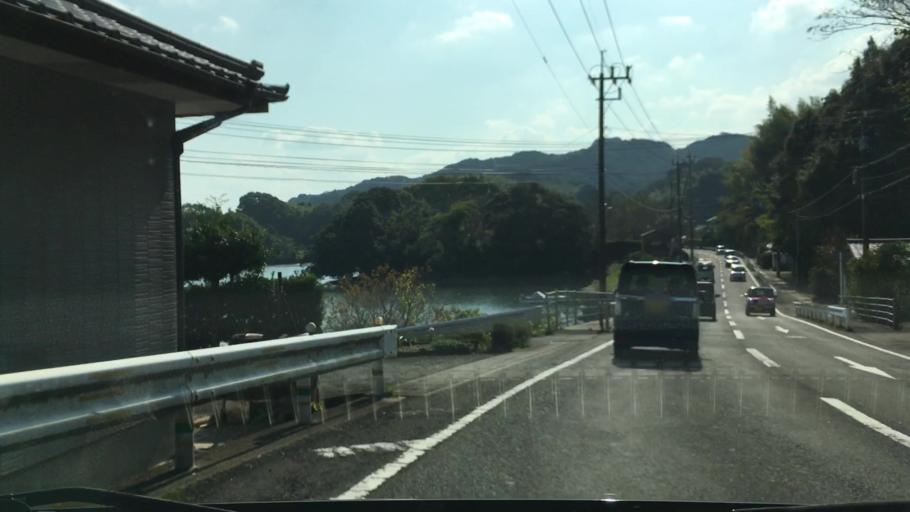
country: JP
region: Nagasaki
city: Togitsu
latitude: 32.9362
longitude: 129.7841
